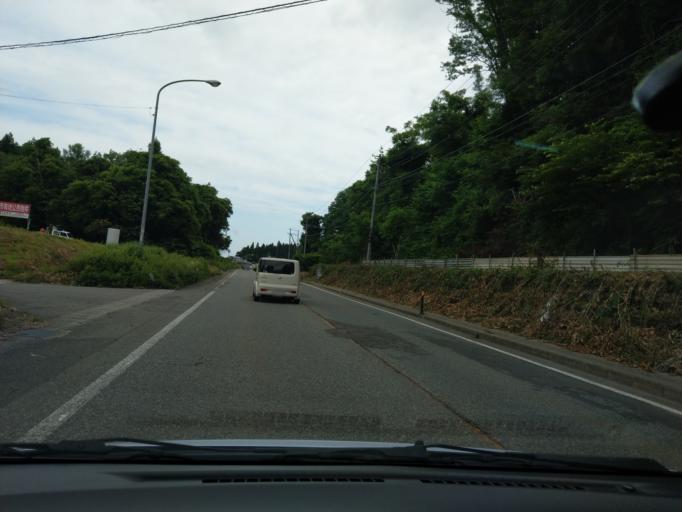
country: JP
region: Akita
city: Yokotemachi
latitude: 39.3388
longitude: 140.5604
